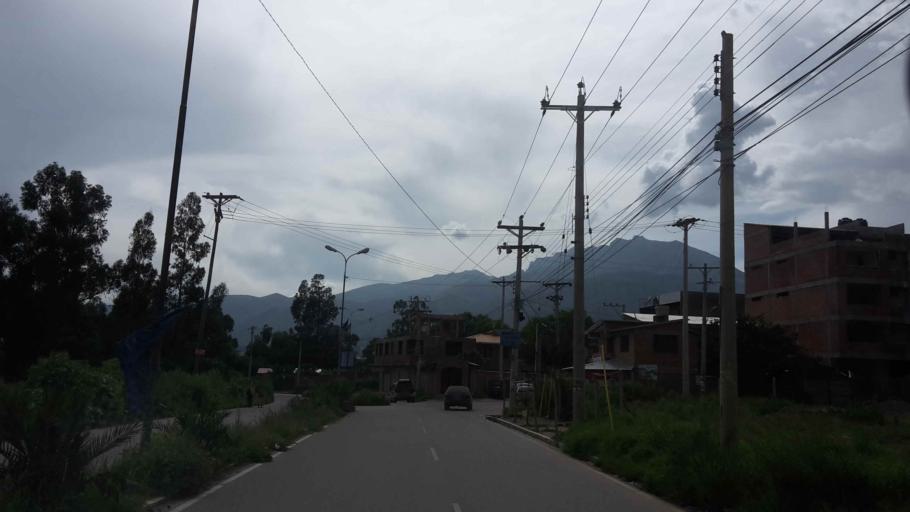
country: BO
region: Cochabamba
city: Cochabamba
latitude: -17.3288
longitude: -66.2458
